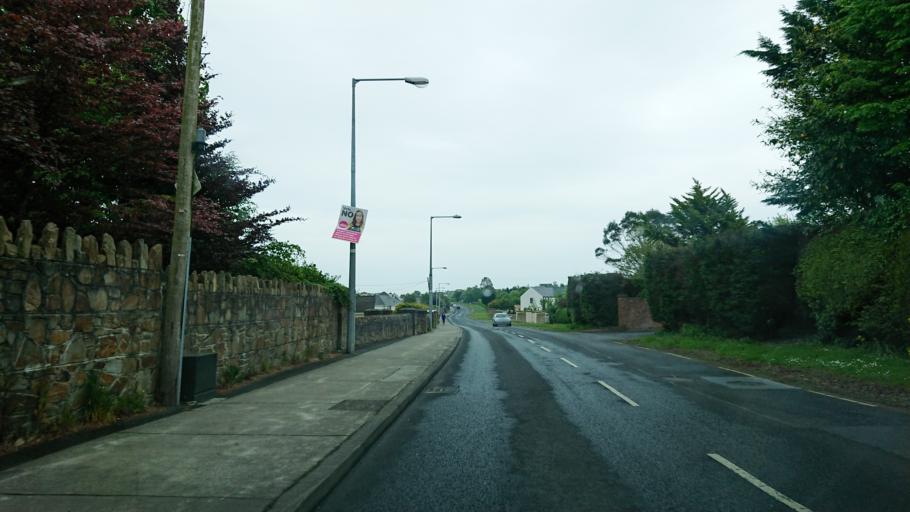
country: IE
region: Munster
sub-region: Waterford
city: Waterford
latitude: 52.2325
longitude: -7.0708
